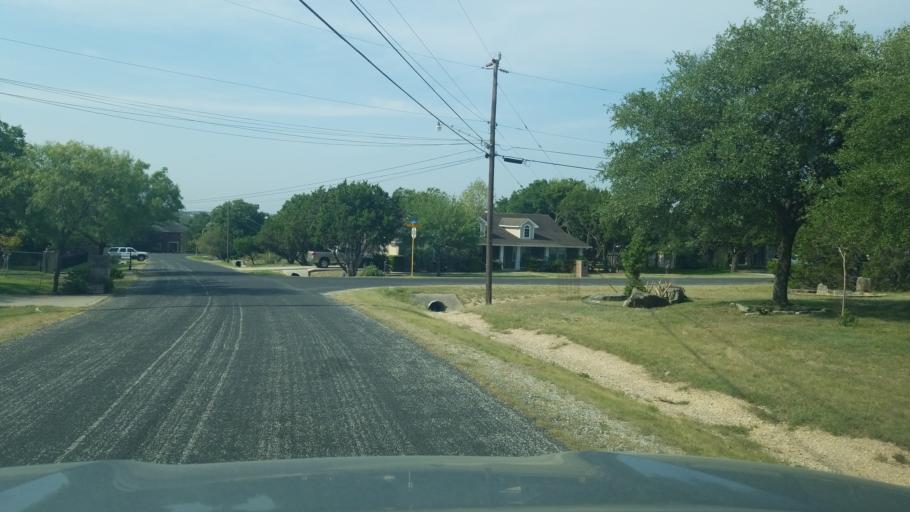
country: US
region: Texas
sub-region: Bexar County
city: Timberwood Park
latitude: 29.7012
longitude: -98.4954
